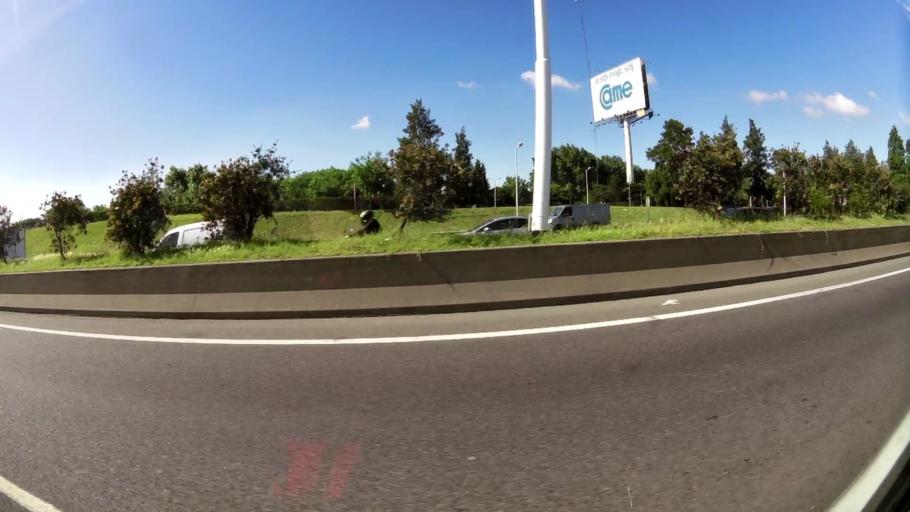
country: AR
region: Buenos Aires
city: Caseros
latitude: -34.6296
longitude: -58.5567
